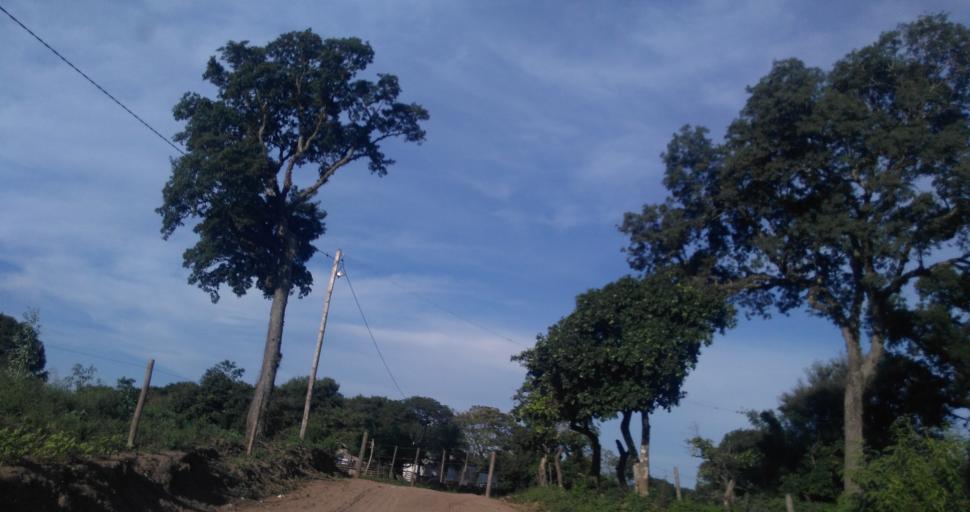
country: AR
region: Chaco
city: Fontana
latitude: -27.4099
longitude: -59.0230
